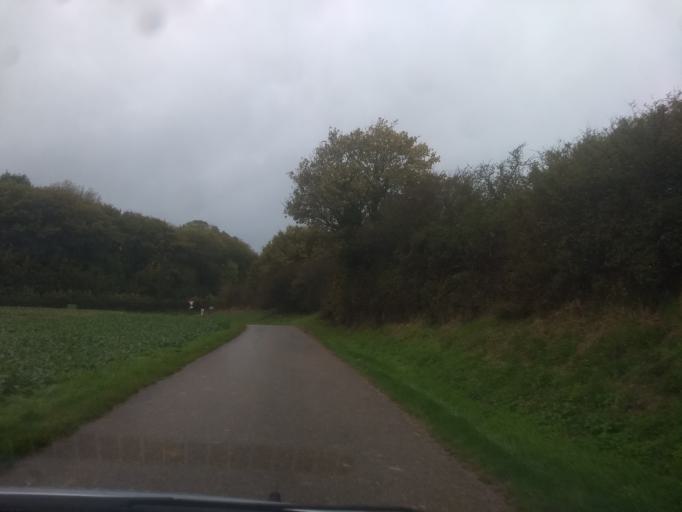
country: FR
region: Nord-Pas-de-Calais
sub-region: Departement du Pas-de-Calais
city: Wissant
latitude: 50.8949
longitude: 1.6875
